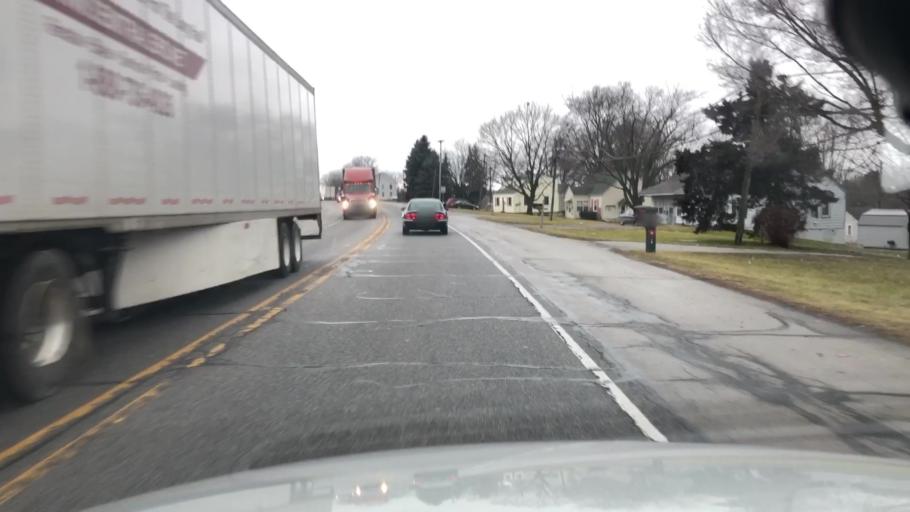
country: US
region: Indiana
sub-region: Allen County
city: New Haven
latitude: 41.0664
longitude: -85.0044
